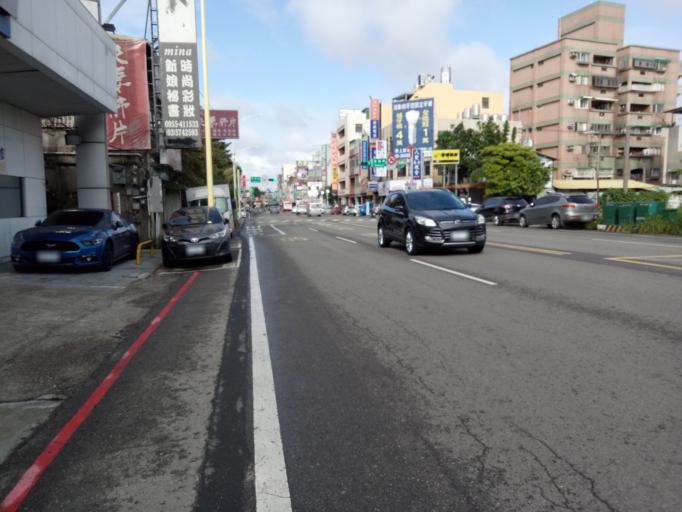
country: TW
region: Taiwan
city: Taoyuan City
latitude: 24.9676
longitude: 121.3011
